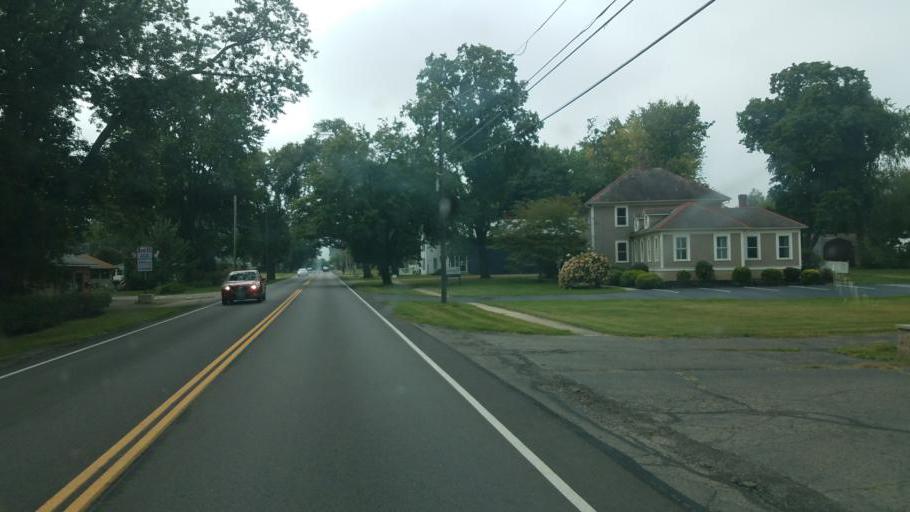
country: US
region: Ohio
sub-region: Knox County
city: Mount Vernon
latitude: 40.3784
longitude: -82.4834
